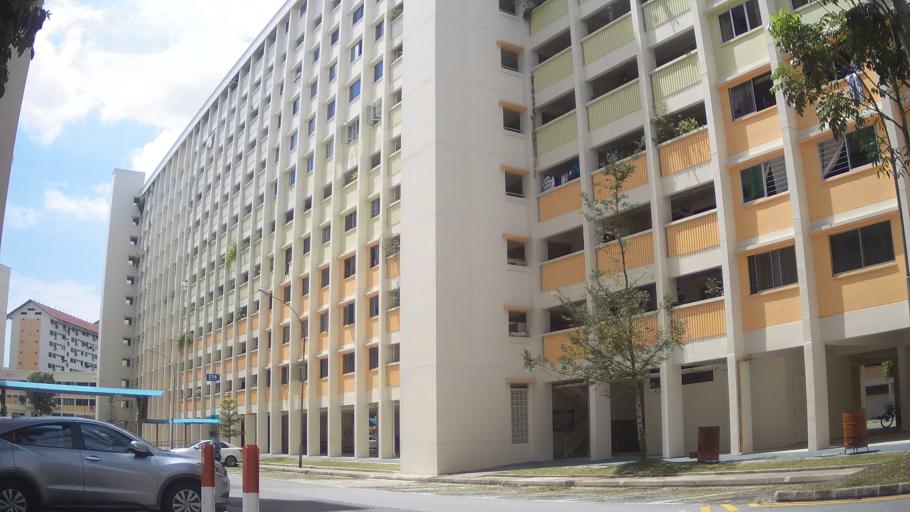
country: MY
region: Johor
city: Johor Bahru
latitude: 1.3769
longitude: 103.7755
